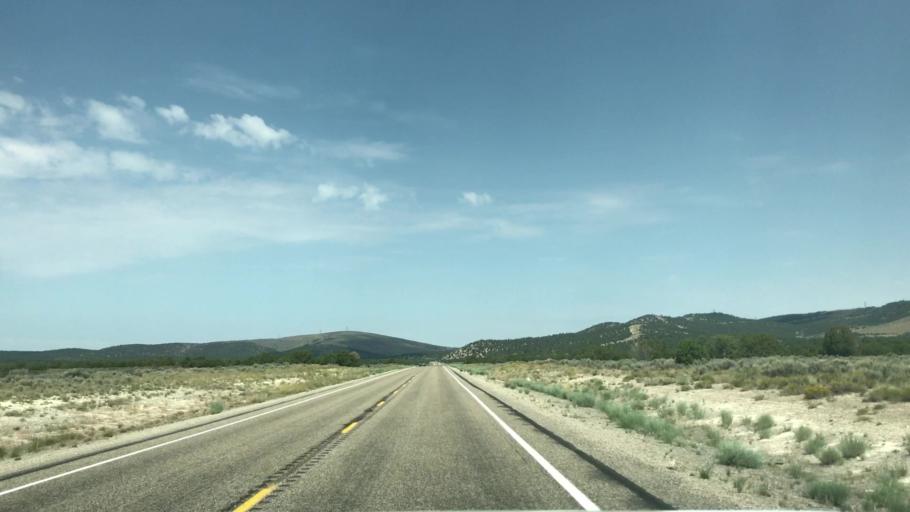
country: US
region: Nevada
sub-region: White Pine County
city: Ely
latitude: 39.3687
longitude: -115.0553
